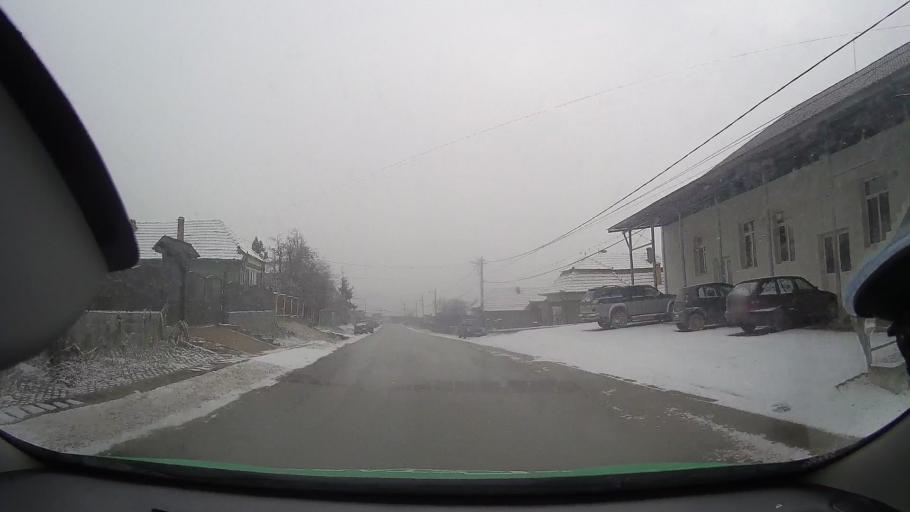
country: RO
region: Alba
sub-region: Comuna Lopadea Noua
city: Lopadea Noua
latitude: 46.2920
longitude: 23.8194
